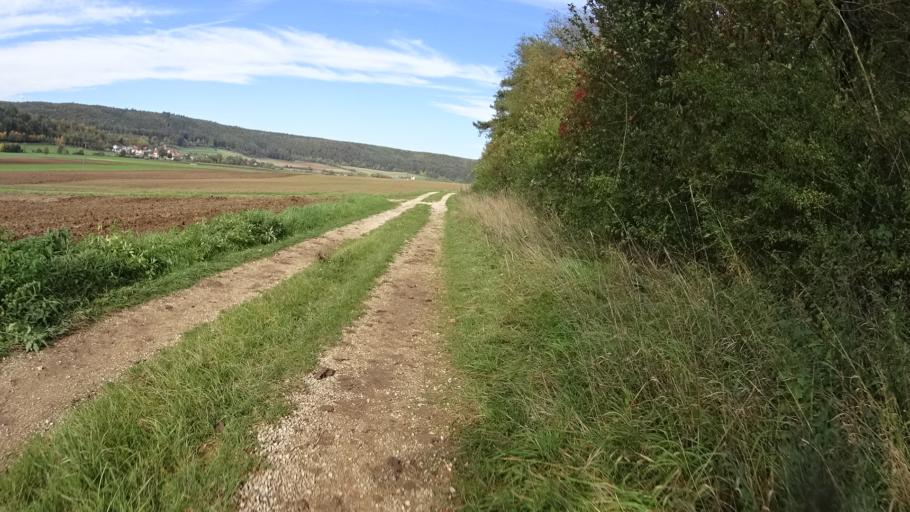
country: DE
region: Bavaria
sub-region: Upper Bavaria
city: Walting
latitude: 48.9227
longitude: 11.3095
